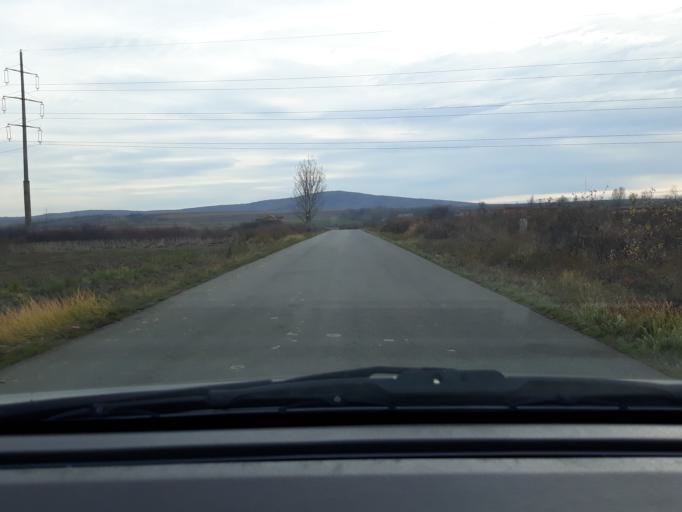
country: RO
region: Bihor
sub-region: Comuna Sanmartin
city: Sanmartin
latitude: 47.0212
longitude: 22.0055
